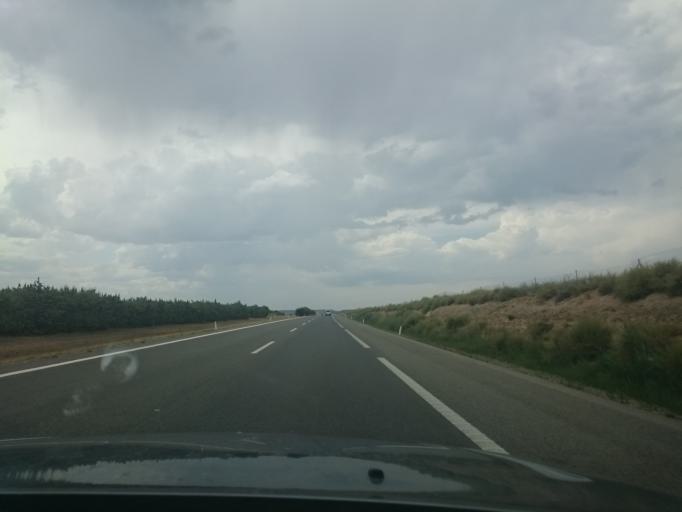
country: ES
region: Navarre
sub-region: Provincia de Navarra
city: Murchante
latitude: 42.0451
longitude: -1.6629
